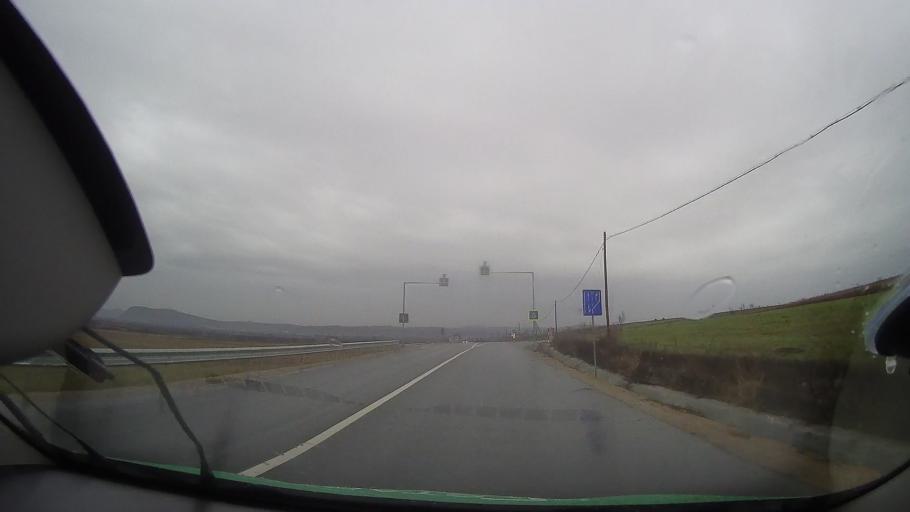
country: RO
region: Bihor
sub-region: Comuna Pocola
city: Pocola
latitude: 46.6826
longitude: 22.3086
